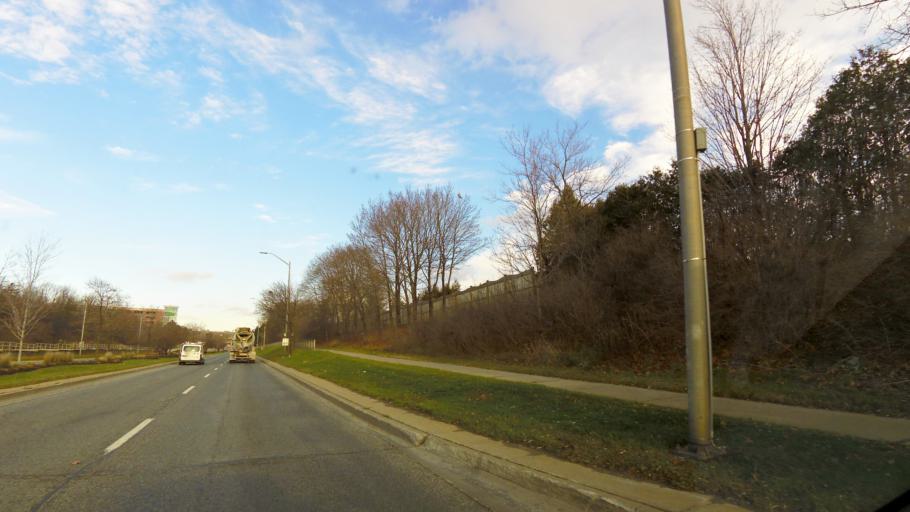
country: CA
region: Ontario
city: Mississauga
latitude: 43.5641
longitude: -79.6690
